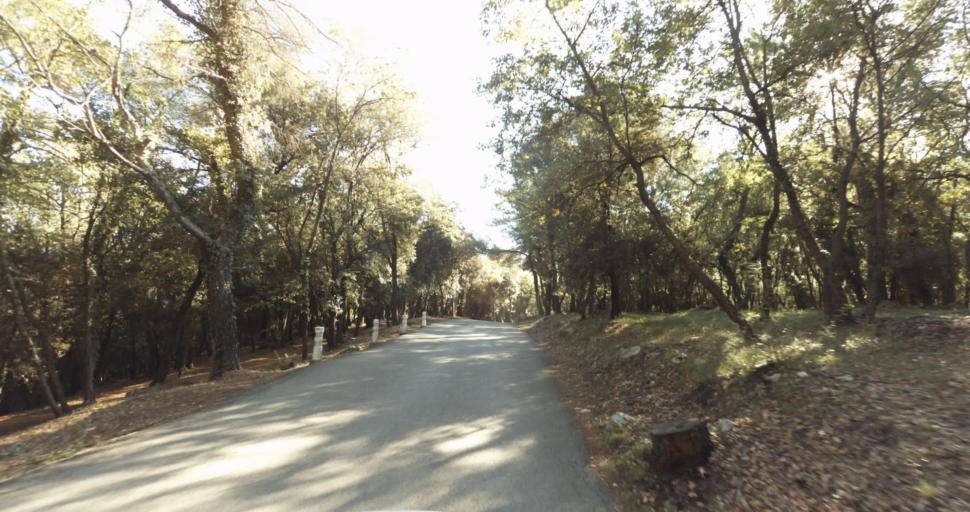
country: FR
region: Provence-Alpes-Cote d'Azur
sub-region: Departement des Alpes-Maritimes
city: Vence
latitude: 43.7133
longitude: 7.0961
